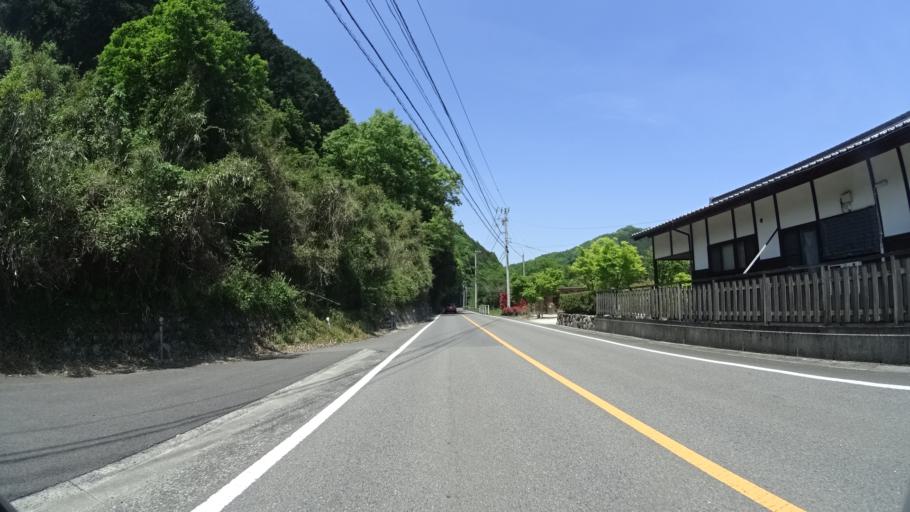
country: JP
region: Ehime
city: Hojo
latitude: 33.9822
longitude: 132.9066
